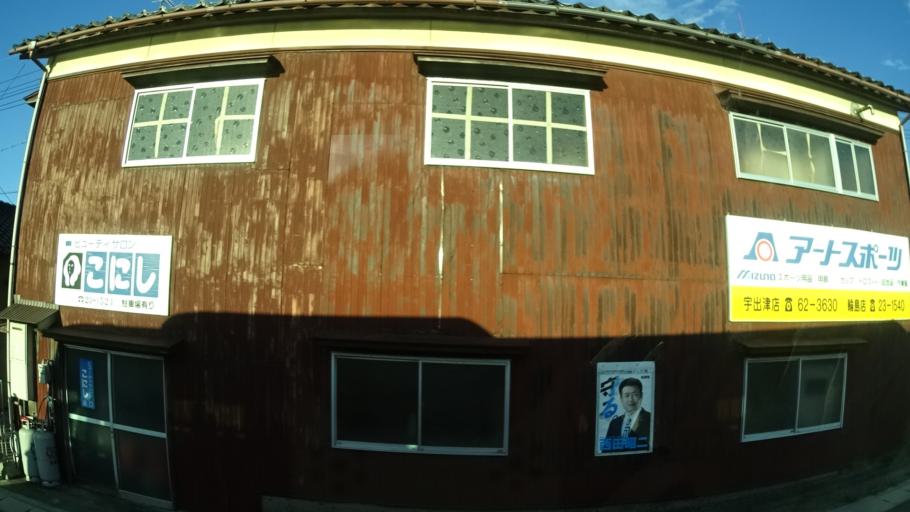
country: JP
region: Ishikawa
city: Nanao
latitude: 37.3914
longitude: 136.9006
